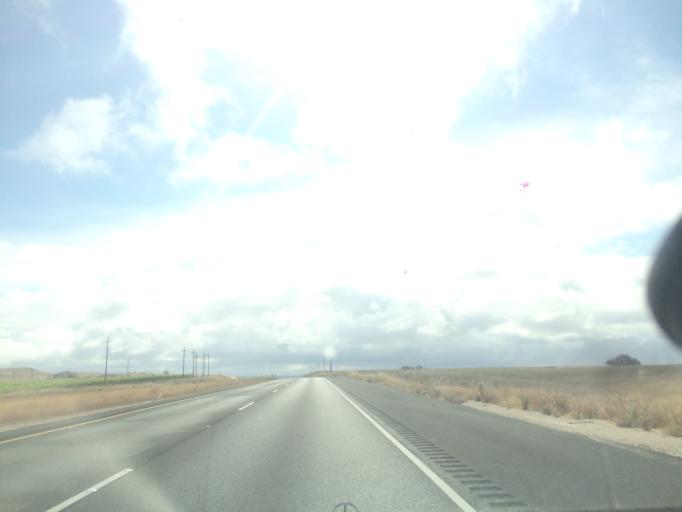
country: US
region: California
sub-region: San Luis Obispo County
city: Shandon
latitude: 35.6588
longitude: -120.4843
